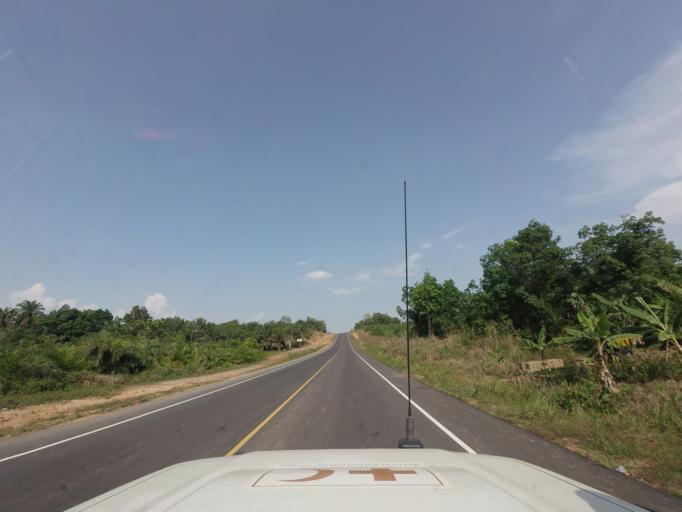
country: LR
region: Margibi
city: Kakata
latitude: 6.7647
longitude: -10.0484
